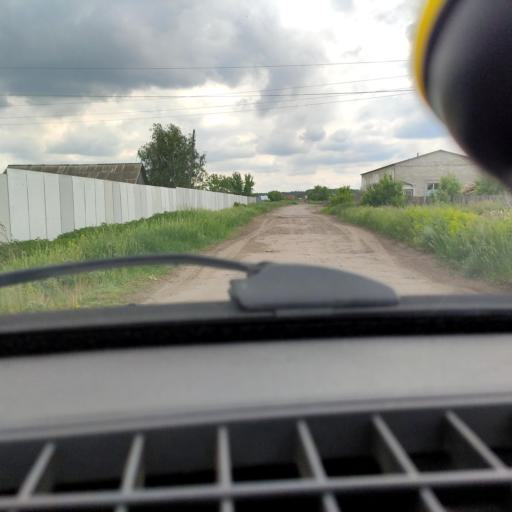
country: RU
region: Samara
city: Povolzhskiy
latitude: 53.6516
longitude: 49.6959
